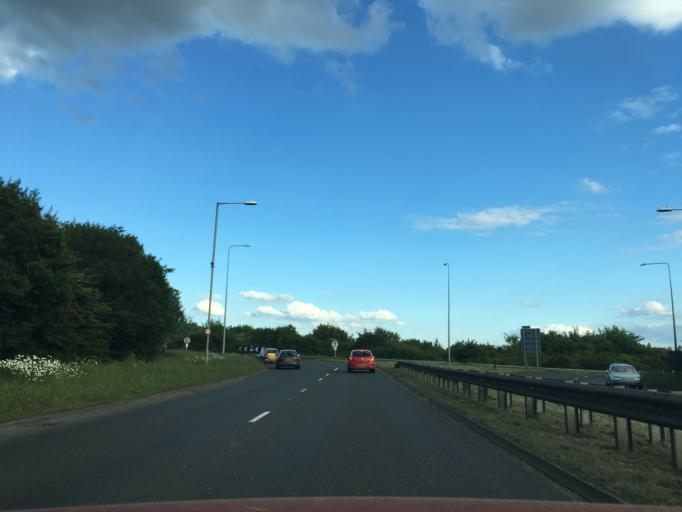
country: GB
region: England
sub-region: Worcestershire
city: Worcester
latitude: 52.1700
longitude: -2.1820
